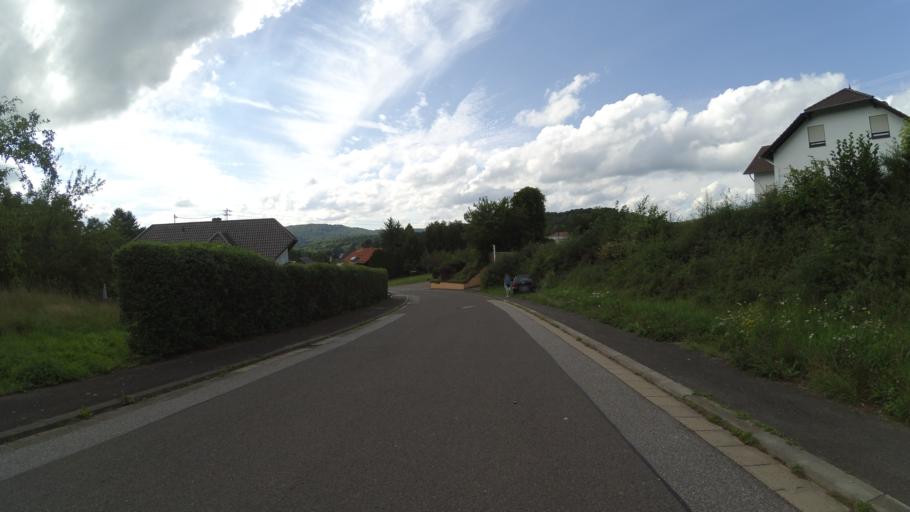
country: DE
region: Rheinland-Pfalz
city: Neuhutten
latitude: 49.5813
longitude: 7.0021
